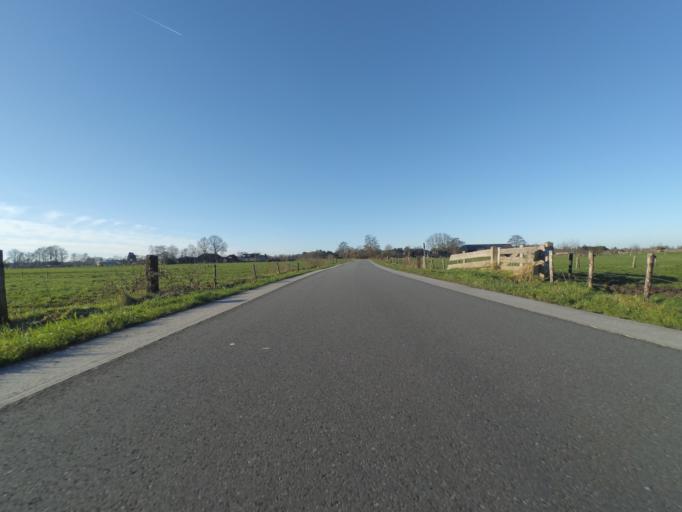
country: NL
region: Gelderland
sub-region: Gemeente Putten
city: Putten
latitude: 52.2450
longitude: 5.5675
